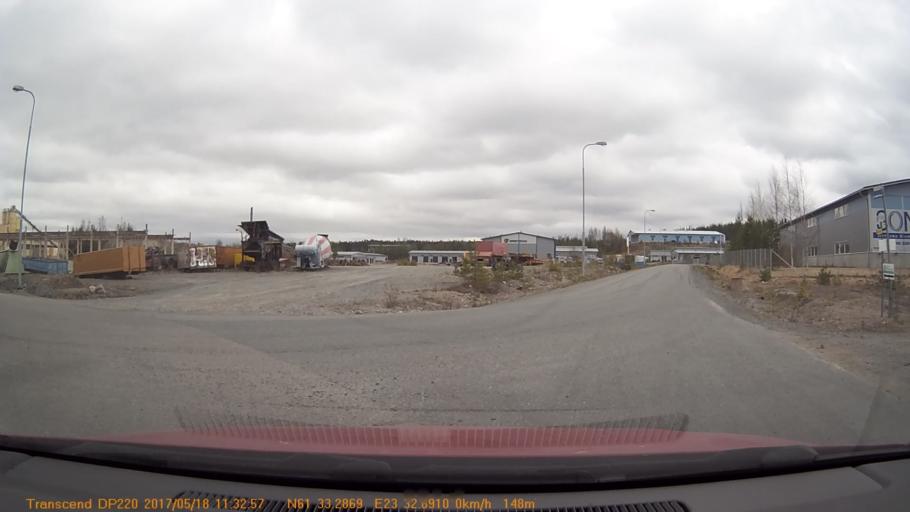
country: FI
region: Pirkanmaa
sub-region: Tampere
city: Yloejaervi
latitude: 61.5549
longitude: 23.5447
